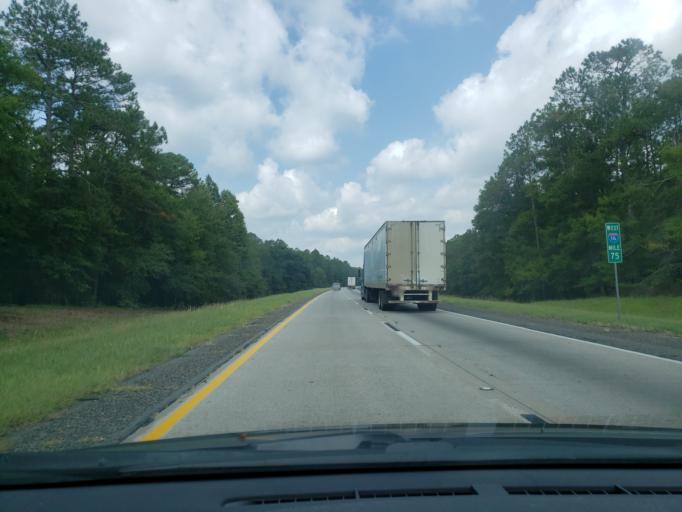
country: US
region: Georgia
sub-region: Treutlen County
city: Soperton
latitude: 32.4265
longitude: -82.5460
